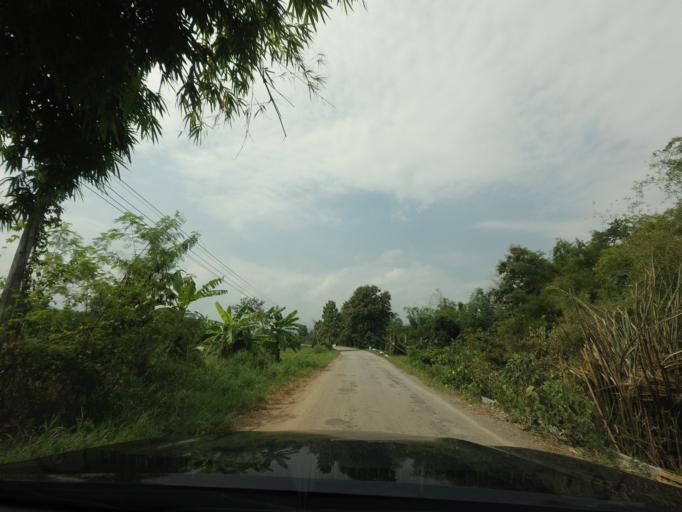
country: LA
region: Xiagnabouli
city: Muang Kenthao
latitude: 17.6719
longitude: 101.3591
